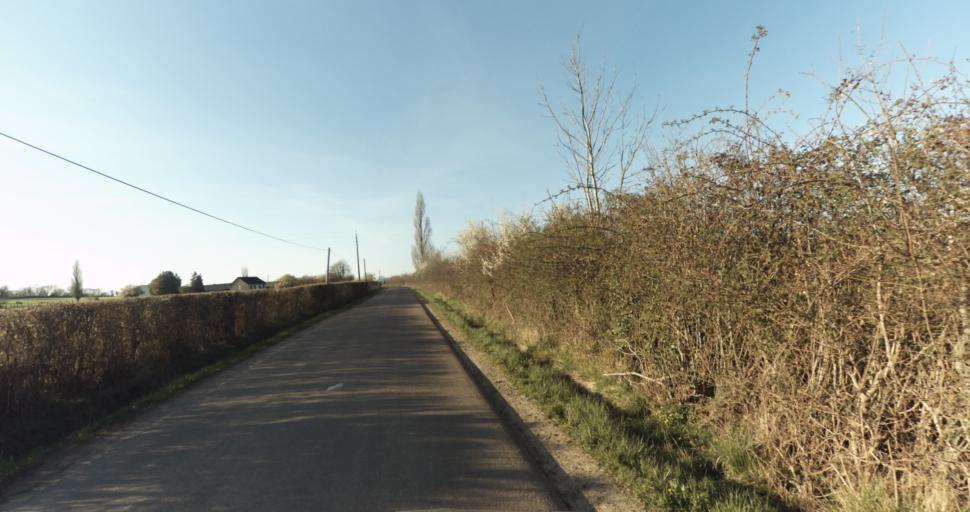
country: FR
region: Lower Normandy
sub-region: Departement du Calvados
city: Saint-Pierre-sur-Dives
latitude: 48.9550
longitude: 0.0097
